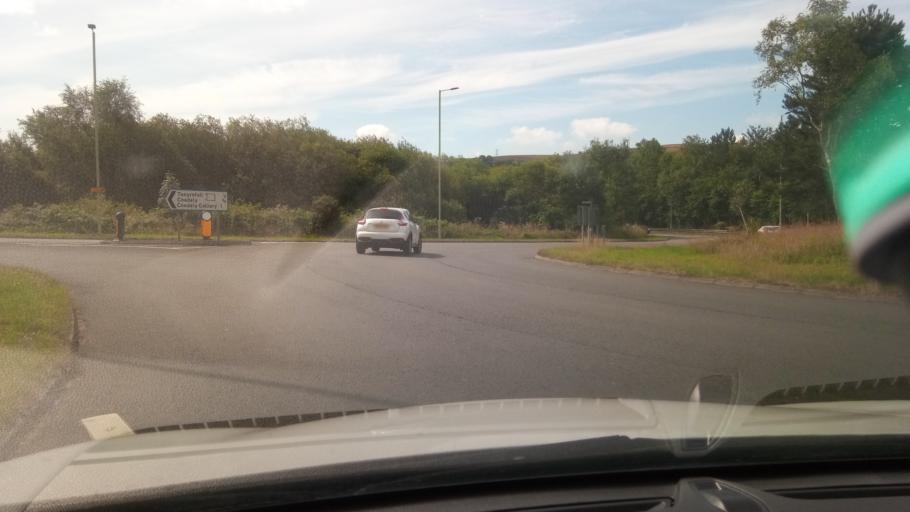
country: GB
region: Wales
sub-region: Rhondda Cynon Taf
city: Tonyrefail
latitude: 51.5769
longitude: -3.4341
